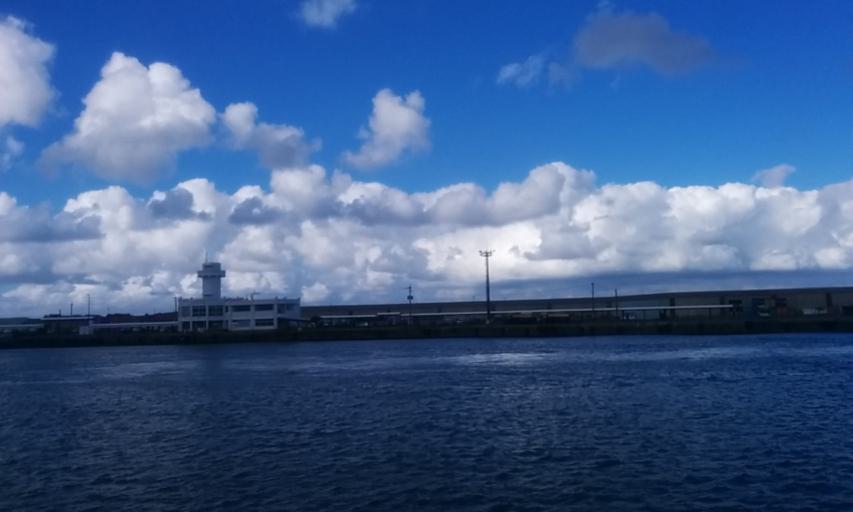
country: JP
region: Kagoshima
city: Nishinoomote
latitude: 30.4304
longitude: 130.5729
